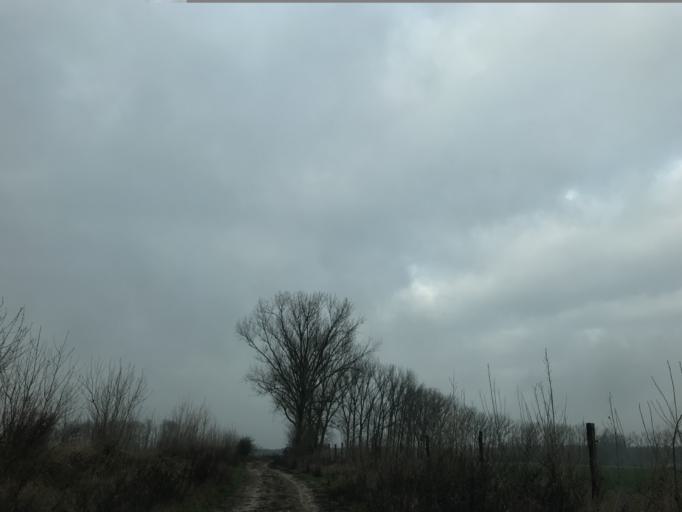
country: DE
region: Brandenburg
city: Kremmen
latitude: 52.7402
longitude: 12.9770
